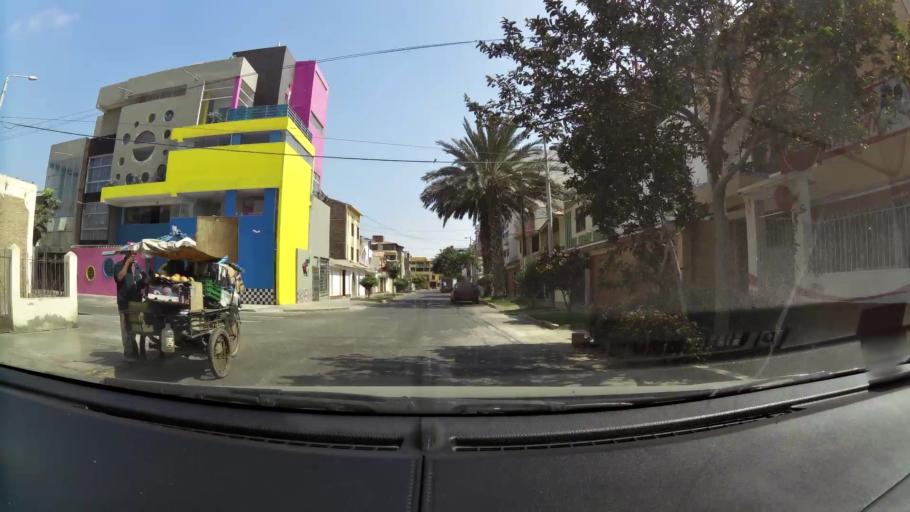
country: PE
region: La Libertad
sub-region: Provincia de Trujillo
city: Buenos Aires
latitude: -8.1263
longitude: -79.0394
